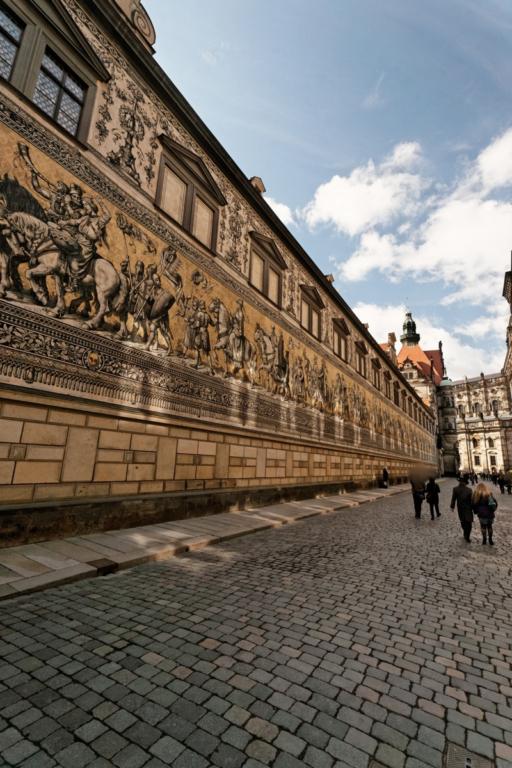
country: DE
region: Saxony
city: Dresden
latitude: 51.0526
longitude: 13.7395
